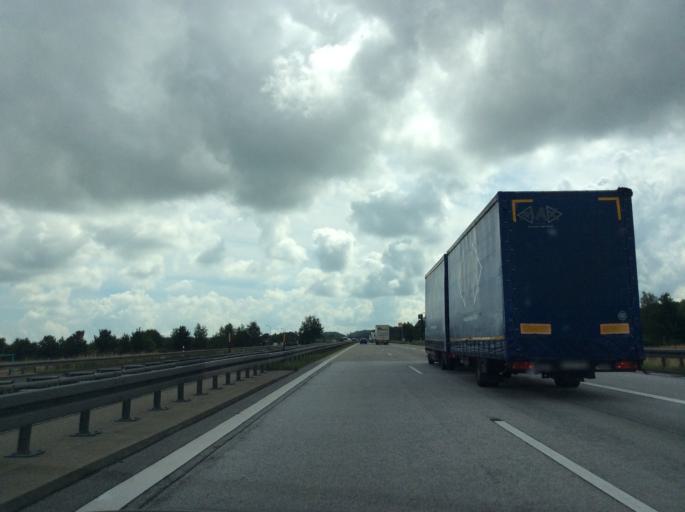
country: DE
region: Brandenburg
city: Jacobsdorf
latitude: 52.3211
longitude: 14.3796
